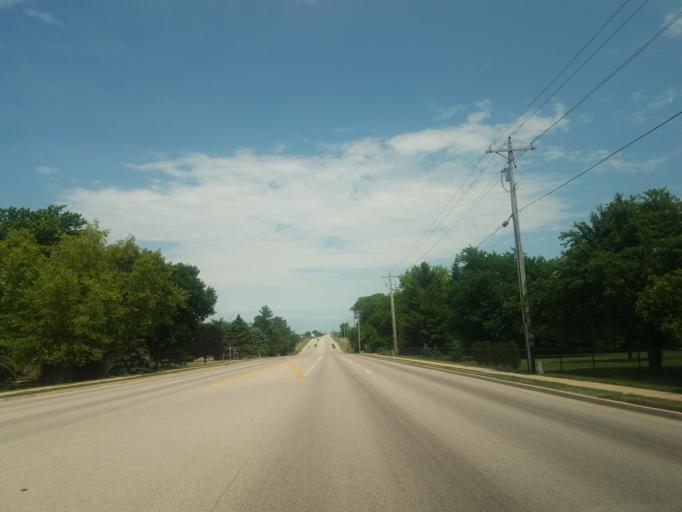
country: US
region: Illinois
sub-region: McLean County
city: Downs
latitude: 40.4233
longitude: -88.9013
